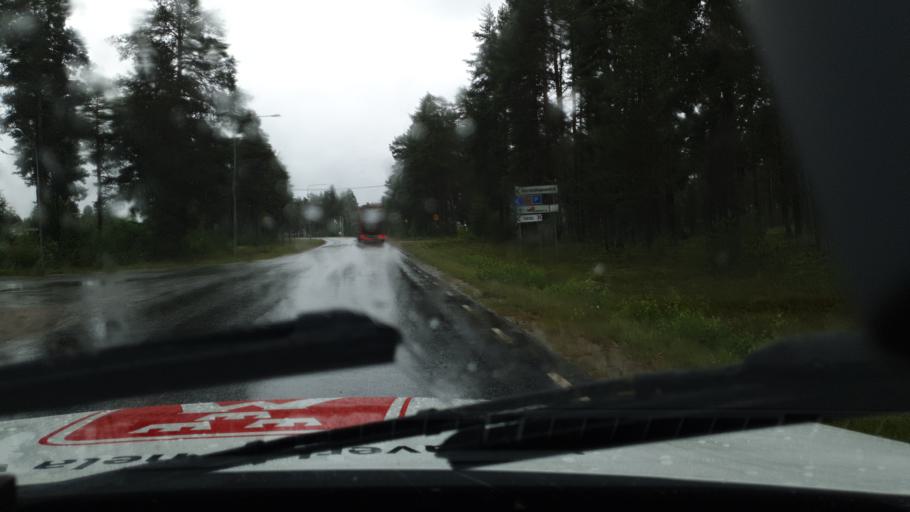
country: SE
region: Vaesterbotten
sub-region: Asele Kommun
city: Asele
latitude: 64.1743
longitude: 17.3605
